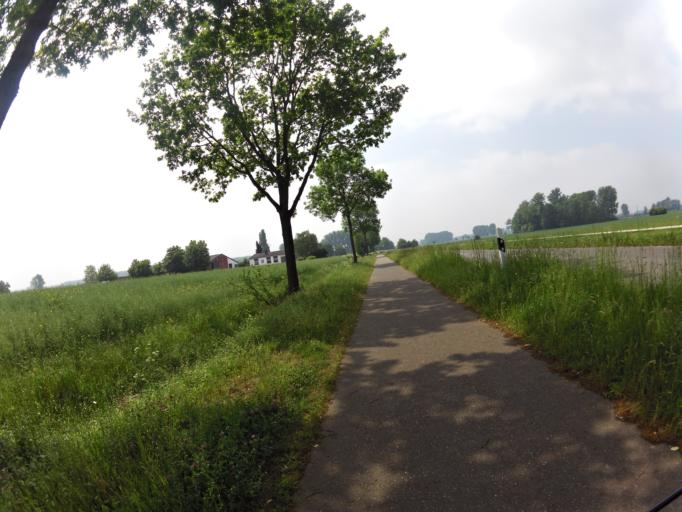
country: DE
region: North Rhine-Westphalia
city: Huckelhoven
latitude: 51.0364
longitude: 6.2040
